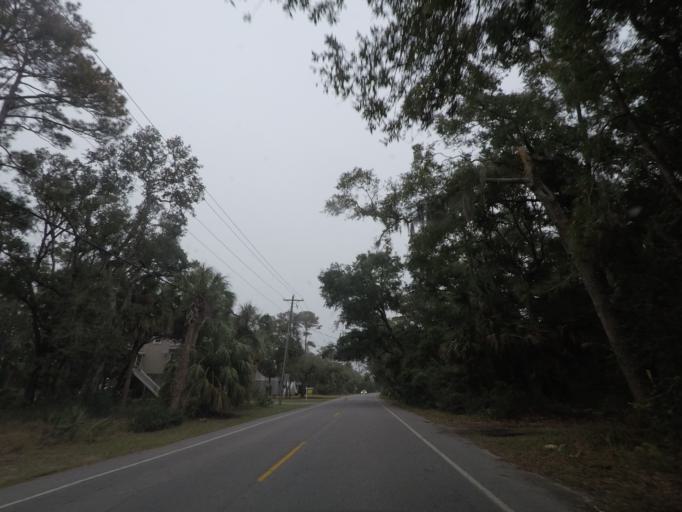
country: US
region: South Carolina
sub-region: Charleston County
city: Seabrook Island
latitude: 32.4953
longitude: -80.3134
